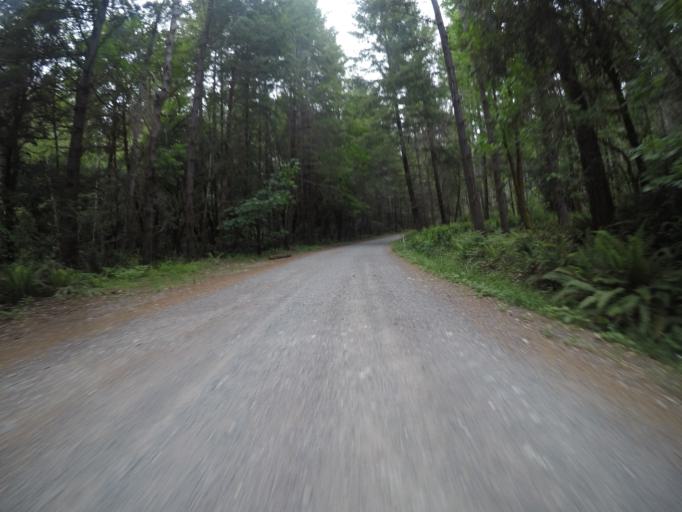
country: US
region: California
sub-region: Del Norte County
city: Bertsch-Oceanview
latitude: 41.6978
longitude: -123.9001
